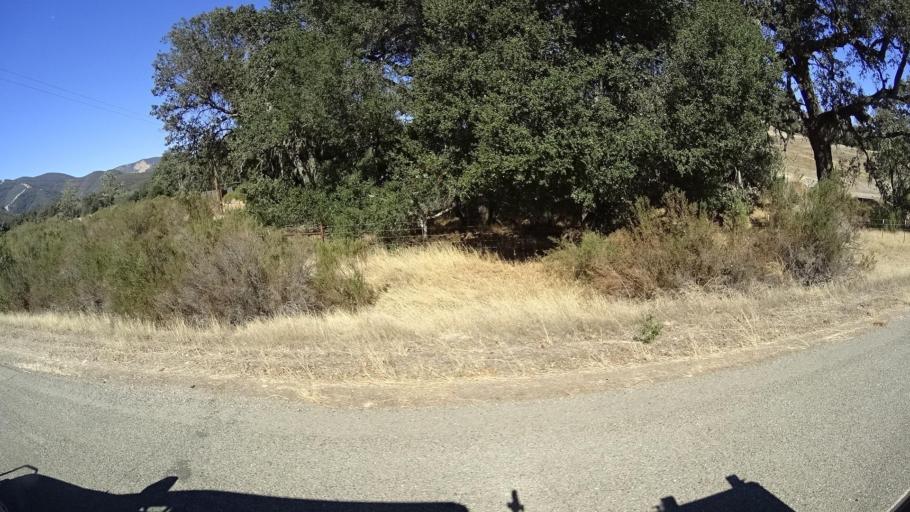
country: US
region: California
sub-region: Monterey County
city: King City
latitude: 36.0971
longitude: -121.1634
